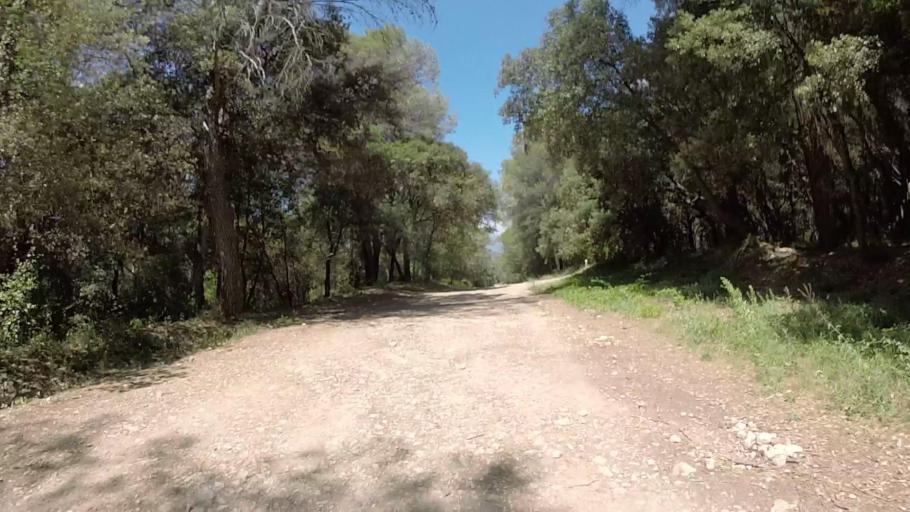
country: FR
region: Provence-Alpes-Cote d'Azur
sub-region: Departement des Alpes-Maritimes
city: Mougins
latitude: 43.5958
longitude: 7.0221
